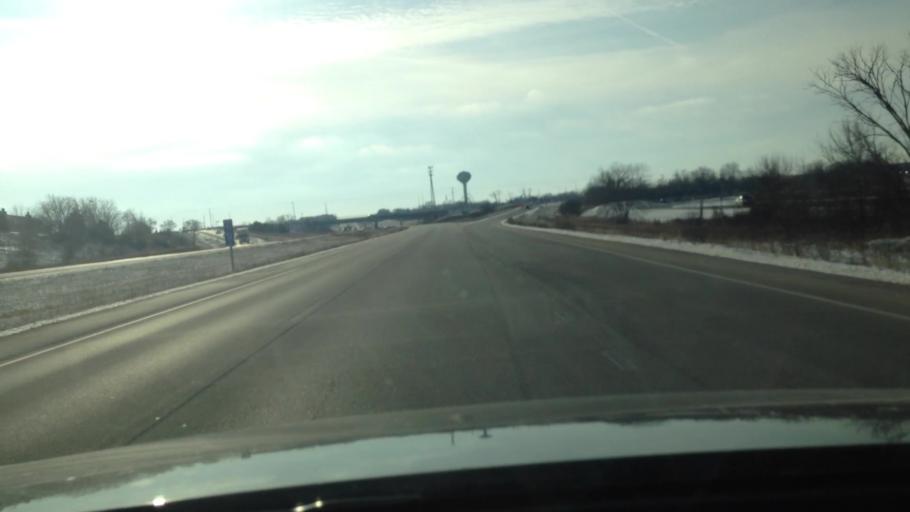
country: US
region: Wisconsin
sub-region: Waukesha County
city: Mukwonago
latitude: 42.8555
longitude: -88.3163
